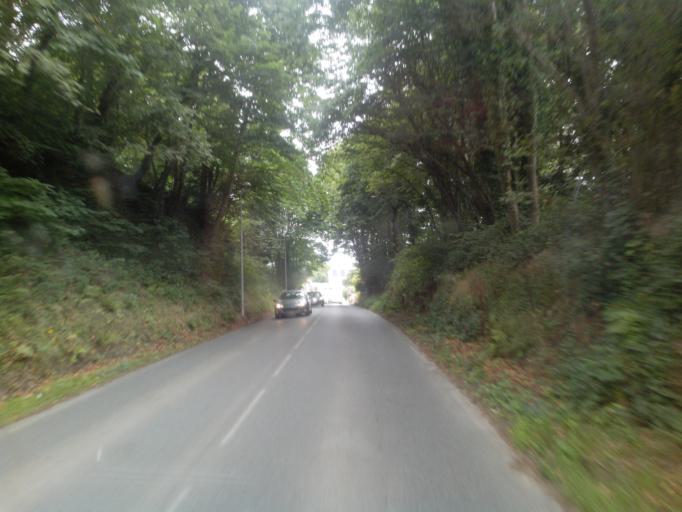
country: FR
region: Brittany
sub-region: Departement des Cotes-d'Armor
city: Paimpol
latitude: 48.7670
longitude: -3.0197
